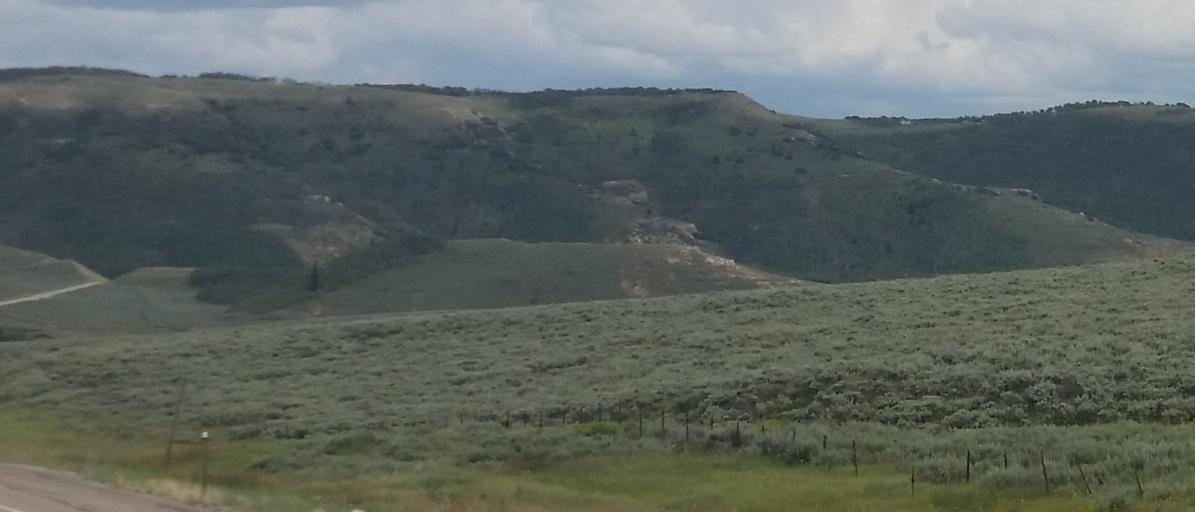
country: US
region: Utah
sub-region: Summit County
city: Francis
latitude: 40.1830
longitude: -111.0510
